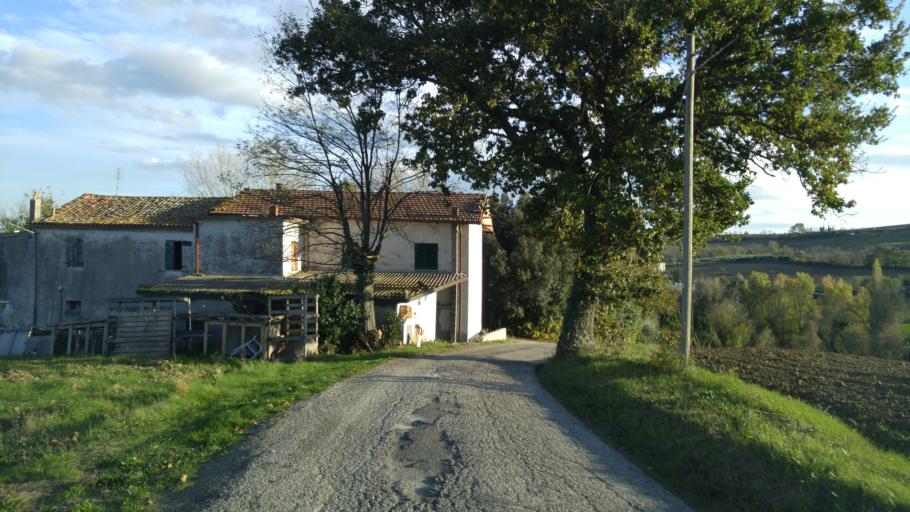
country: IT
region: The Marches
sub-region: Provincia di Pesaro e Urbino
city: Calcinelli
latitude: 43.7788
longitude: 12.9149
